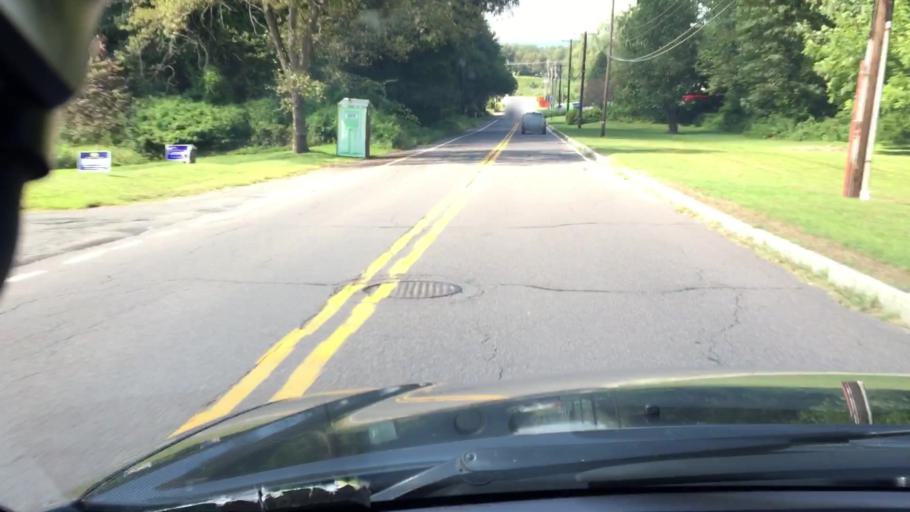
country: US
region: Pennsylvania
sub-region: Luzerne County
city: Nanticoke
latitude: 41.1875
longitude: -75.9873
